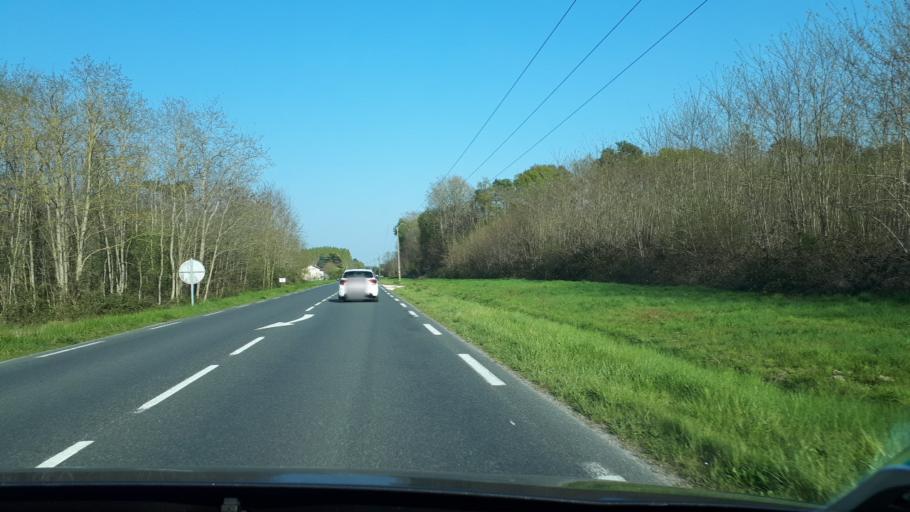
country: FR
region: Centre
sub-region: Departement d'Indre-et-Loire
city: Civray-de-Touraine
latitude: 47.3215
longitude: 1.0450
